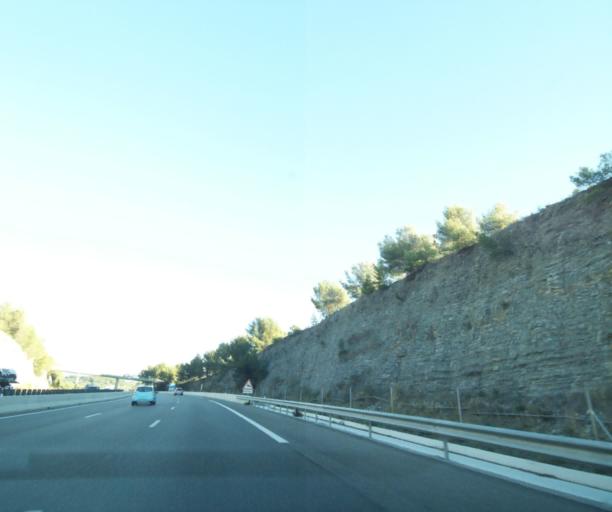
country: FR
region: Provence-Alpes-Cote d'Azur
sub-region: Departement des Bouches-du-Rhone
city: Ceyreste
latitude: 43.1919
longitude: 5.6544
